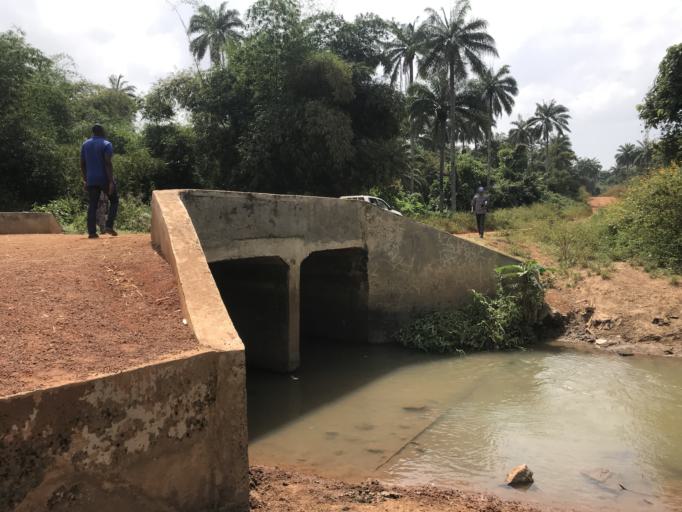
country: NG
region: Osun
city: Ikirun
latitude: 7.9347
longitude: 4.6367
